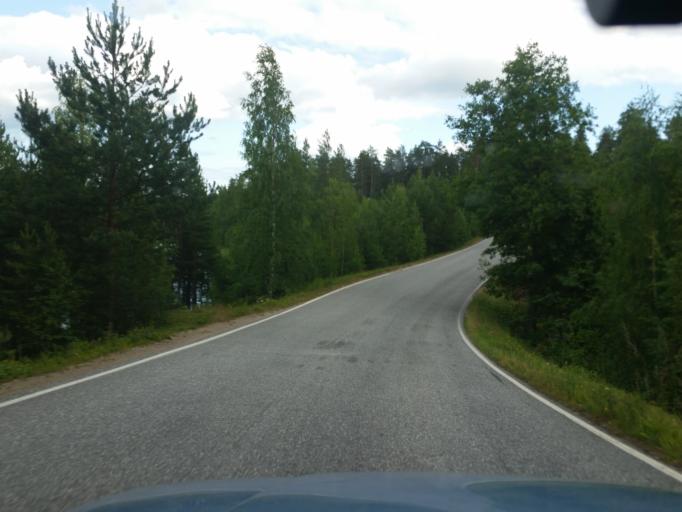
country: FI
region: Southern Savonia
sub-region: Savonlinna
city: Sulkava
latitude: 61.7798
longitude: 28.4262
